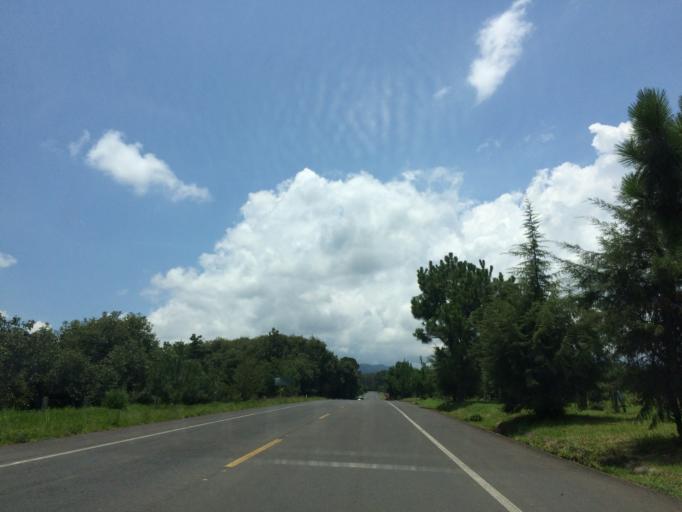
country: MX
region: Michoacan
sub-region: Periban
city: San Francisco Periban
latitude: 19.5560
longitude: -102.3905
